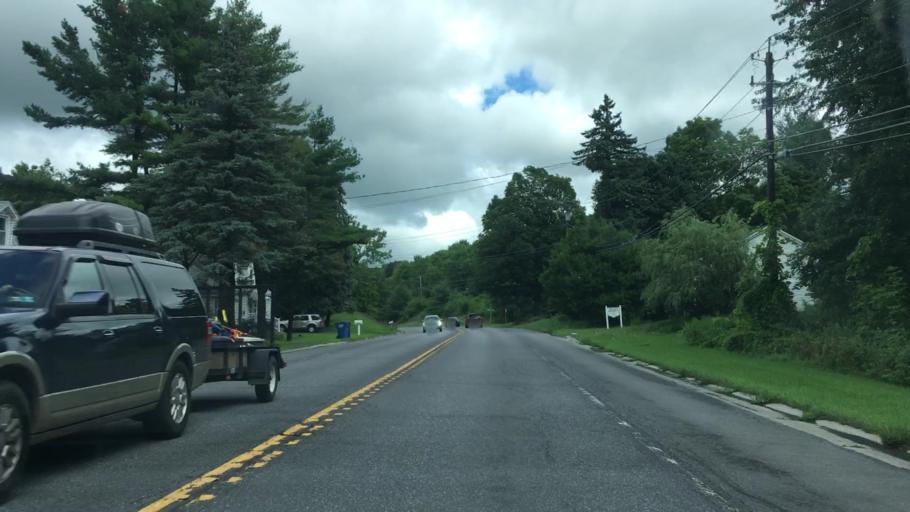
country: US
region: New York
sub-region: Rensselaer County
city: Poestenkill
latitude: 42.7897
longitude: -73.5715
